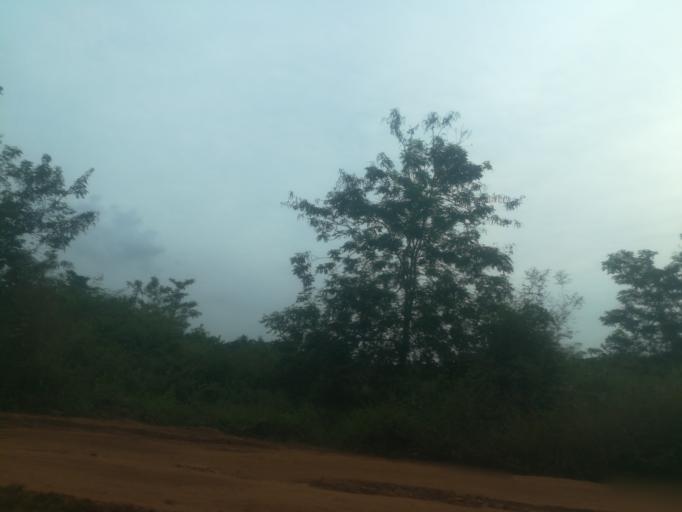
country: NG
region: Ogun
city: Ayetoro
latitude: 7.2135
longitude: 3.1843
